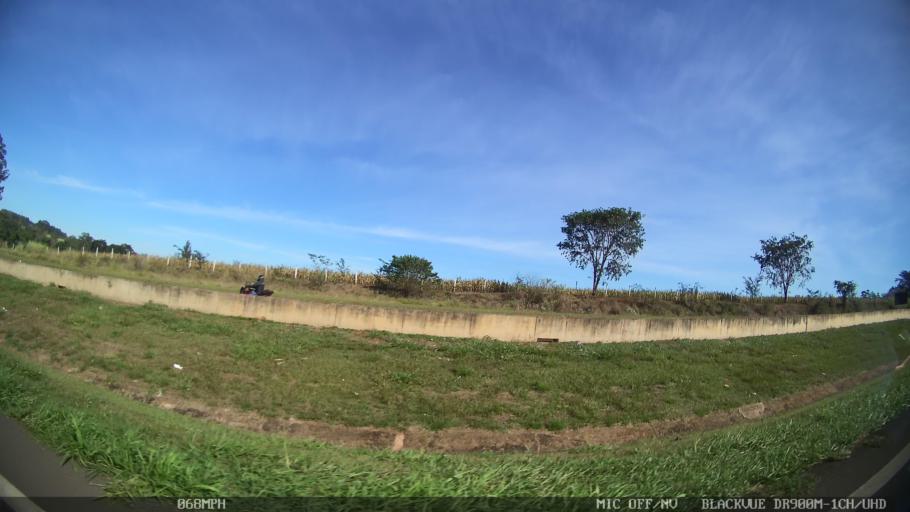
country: BR
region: Sao Paulo
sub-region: Leme
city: Leme
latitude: -22.0969
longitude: -47.4163
